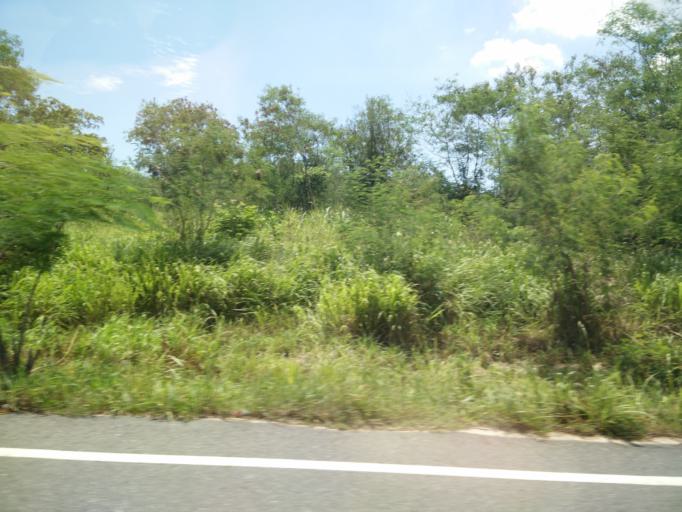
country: TH
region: Chon Buri
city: Phatthaya
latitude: 12.9041
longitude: 100.9874
